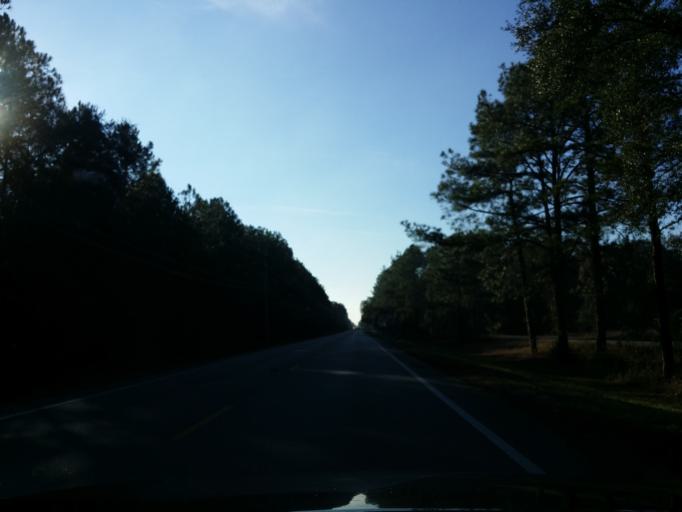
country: US
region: Florida
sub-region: Leon County
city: Woodville
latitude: 30.3642
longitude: -84.2653
